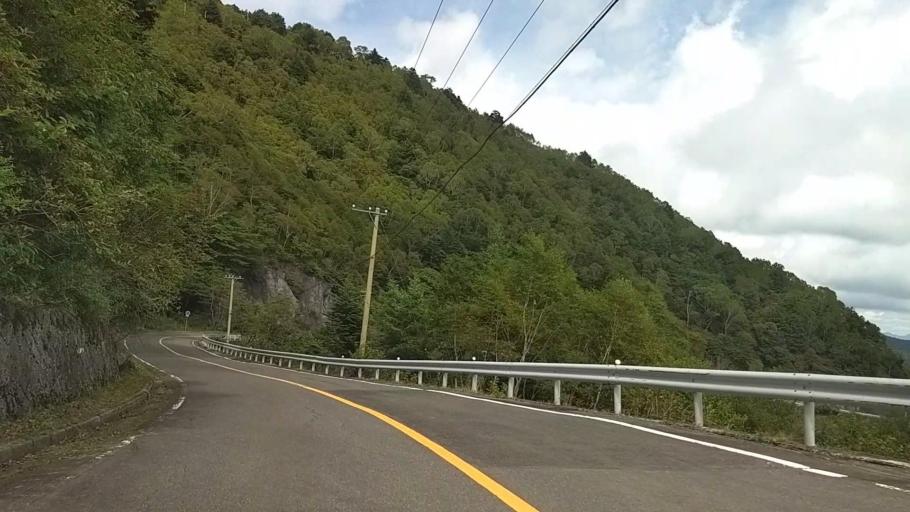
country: JP
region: Tochigi
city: Nikko
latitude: 36.7095
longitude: 139.4802
